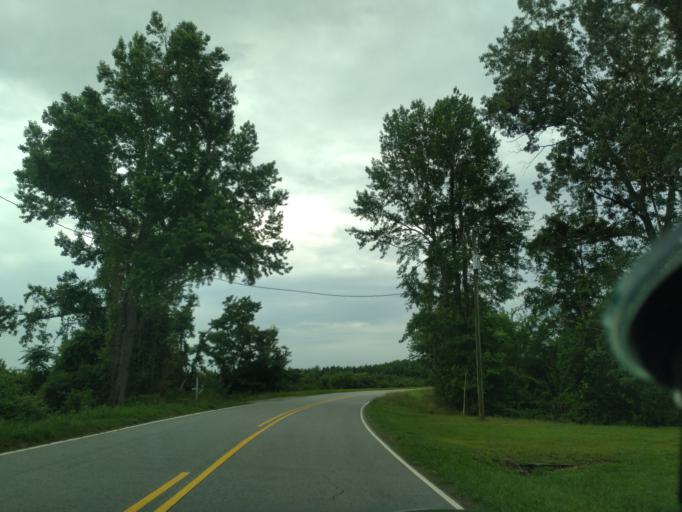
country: US
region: North Carolina
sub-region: Washington County
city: Plymouth
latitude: 35.8765
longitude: -76.6007
